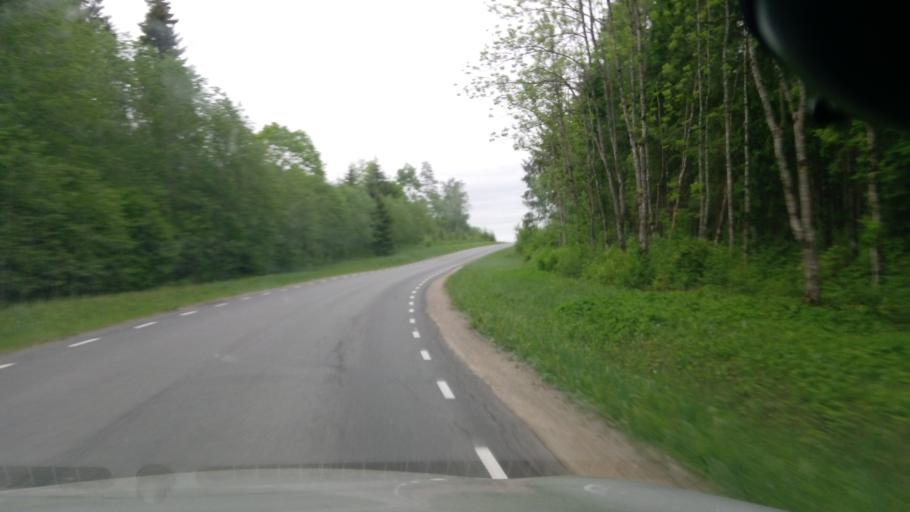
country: EE
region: Jaervamaa
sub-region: Koeru vald
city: Koeru
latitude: 58.9875
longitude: 26.0512
